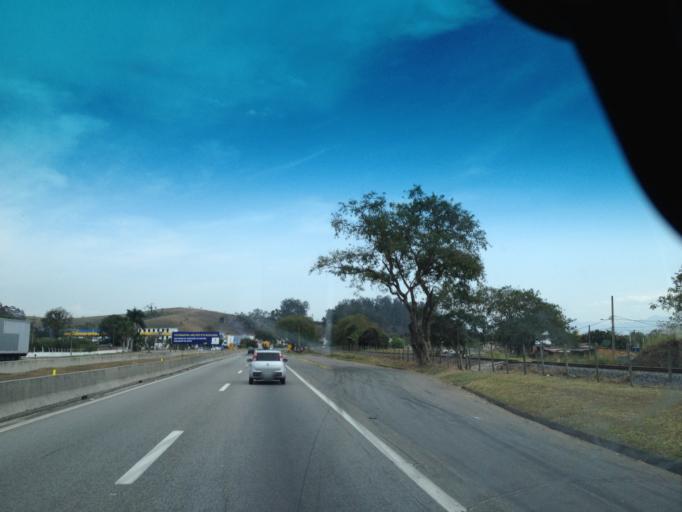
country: BR
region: Rio de Janeiro
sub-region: Porto Real
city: Porto Real
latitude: -22.4647
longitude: -44.2852
